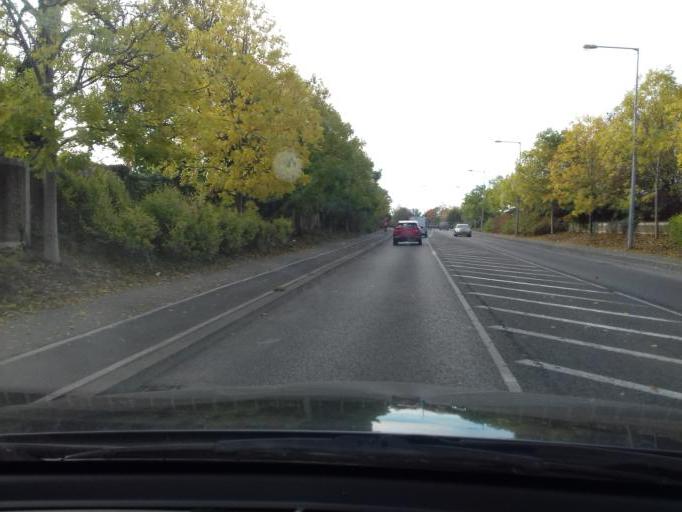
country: IE
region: Leinster
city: Hartstown
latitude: 53.3892
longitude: -6.4136
